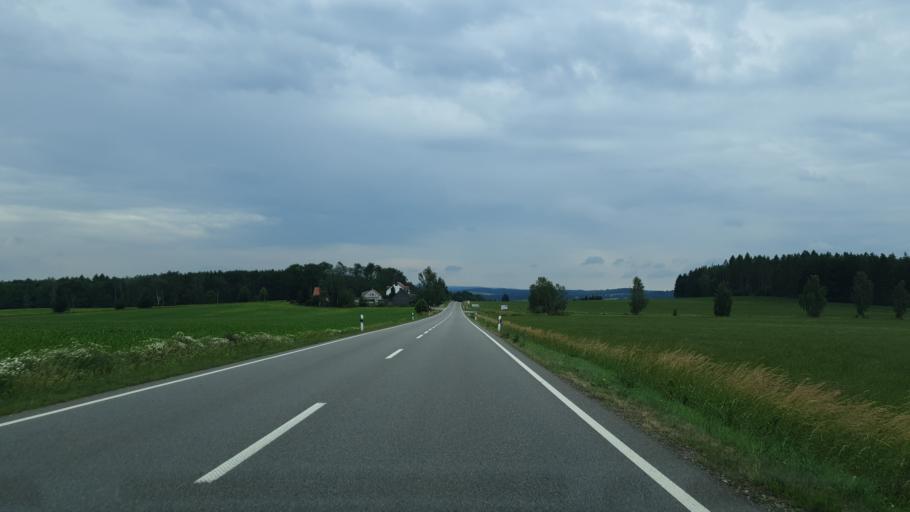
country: DE
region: Saxony
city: Hirschfeld
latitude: 50.6293
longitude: 12.4319
